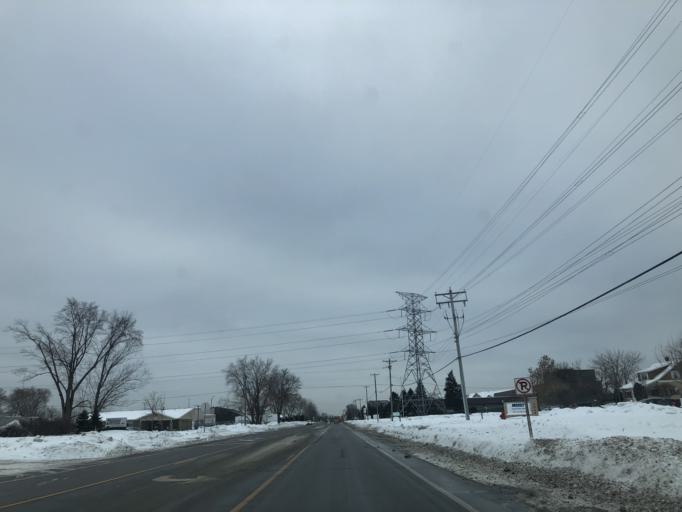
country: US
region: Minnesota
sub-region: Ramsey County
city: New Brighton
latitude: 45.0841
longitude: -93.1883
